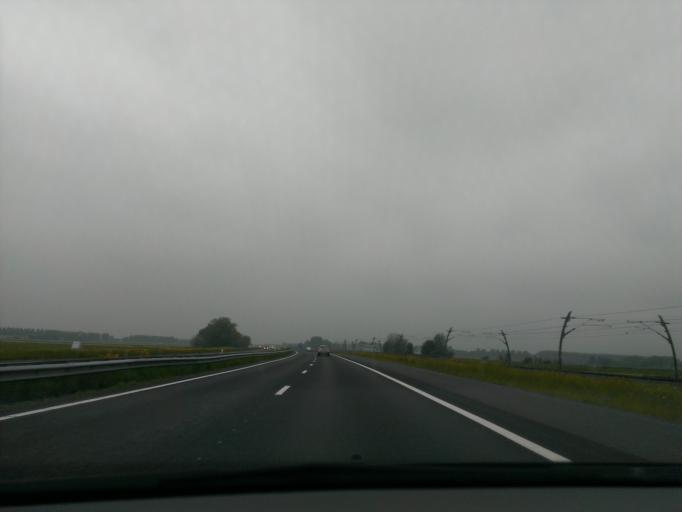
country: NL
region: South Holland
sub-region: Gemeente Leerdam
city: Leerdam
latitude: 51.8475
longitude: 5.1147
